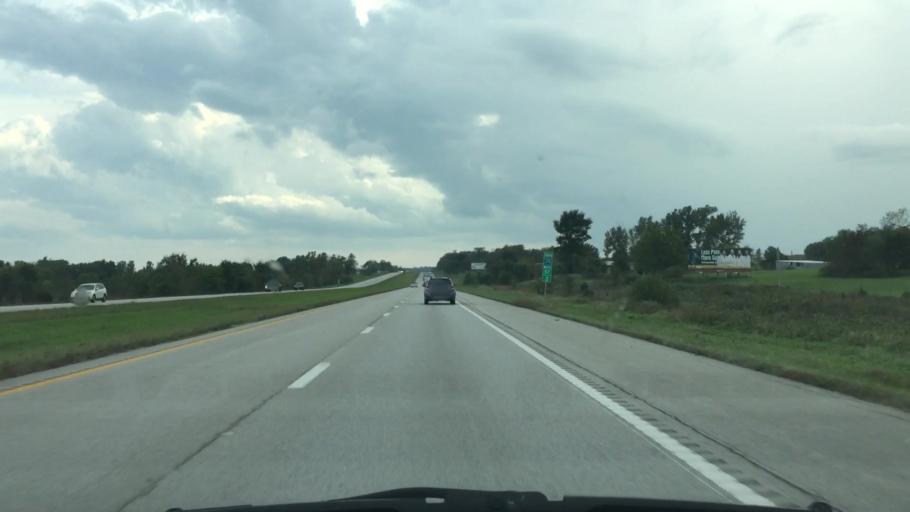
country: US
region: Missouri
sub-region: Clinton County
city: Cameron
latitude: 39.7950
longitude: -94.2028
